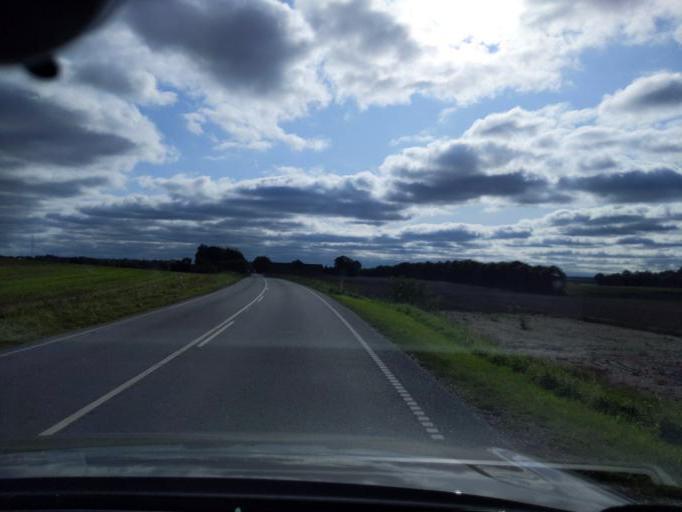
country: DK
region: North Denmark
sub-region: Mariagerfjord Kommune
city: Hobro
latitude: 56.5423
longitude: 9.7257
